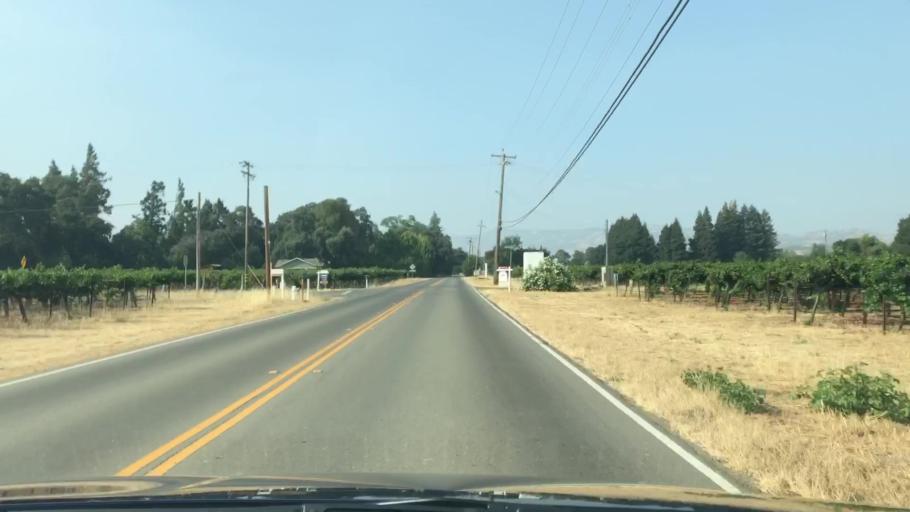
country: US
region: California
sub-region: Solano County
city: Green Valley
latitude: 38.2657
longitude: -122.1132
